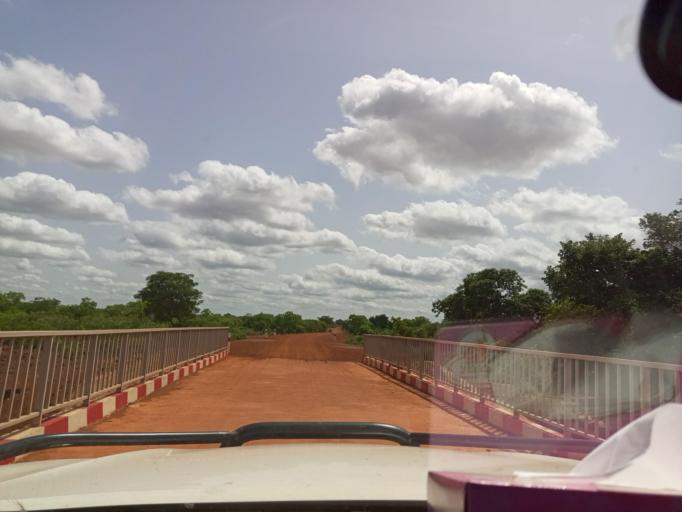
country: ML
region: Sikasso
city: Kolondieba
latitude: 11.5750
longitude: -6.6902
